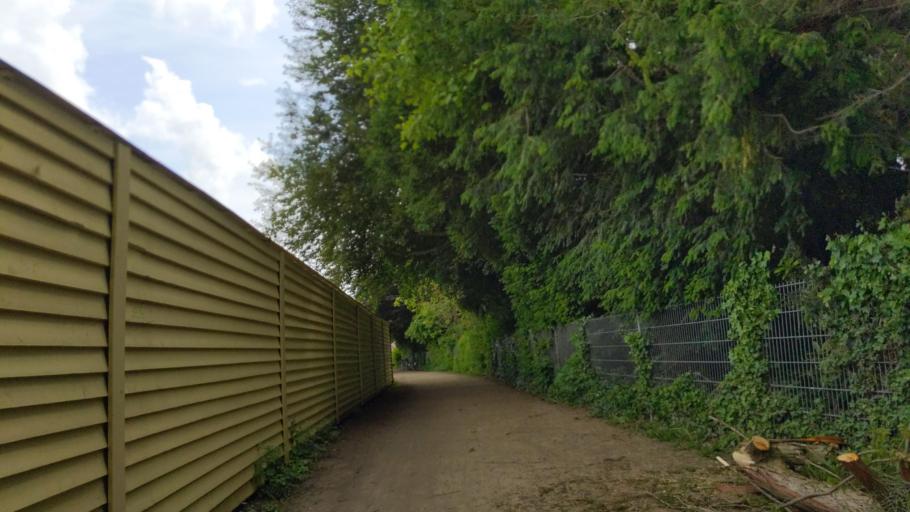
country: DE
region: Schleswig-Holstein
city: Luebeck
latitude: 53.8699
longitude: 10.7041
